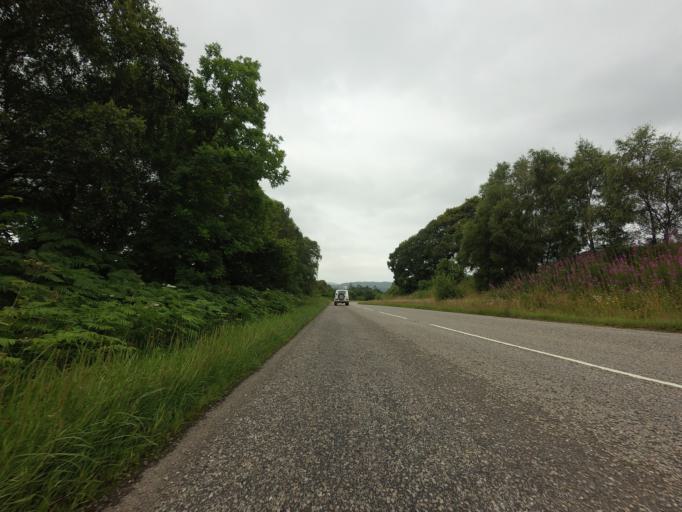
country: GB
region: Scotland
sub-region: Highland
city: Alness
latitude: 57.9095
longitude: -4.3691
